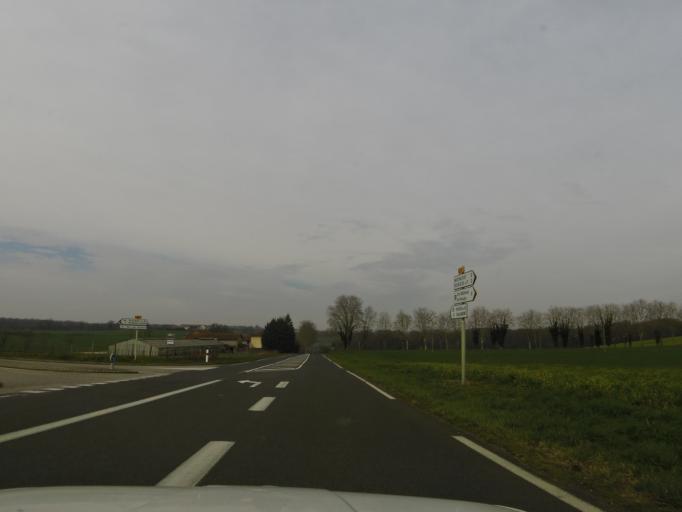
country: FR
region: Rhone-Alpes
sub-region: Departement de l'Ain
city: Perouges
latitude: 45.9492
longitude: 5.1752
